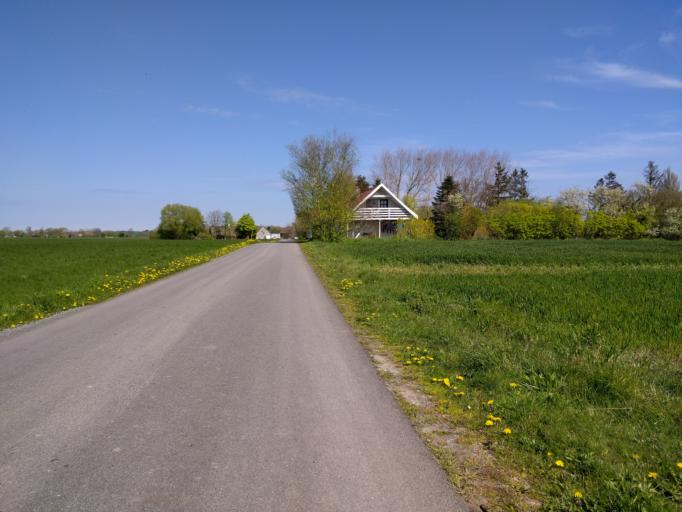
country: DK
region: South Denmark
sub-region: Kerteminde Kommune
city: Munkebo
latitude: 55.4426
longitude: 10.6017
